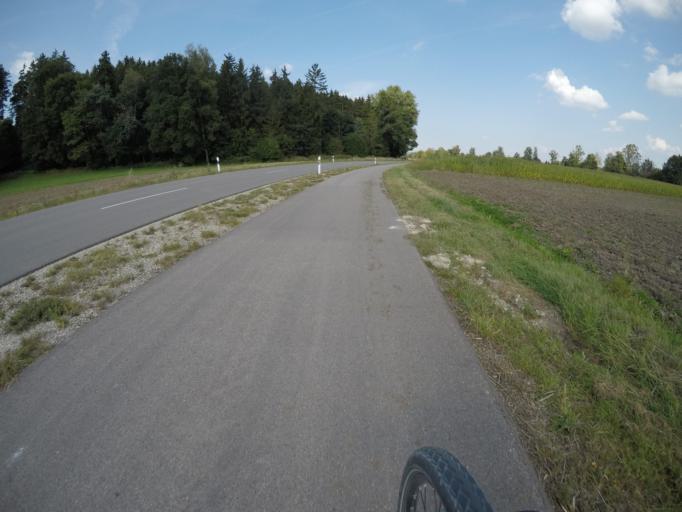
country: DE
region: Bavaria
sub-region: Swabia
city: Kuhlenthal
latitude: 48.5718
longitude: 10.8225
